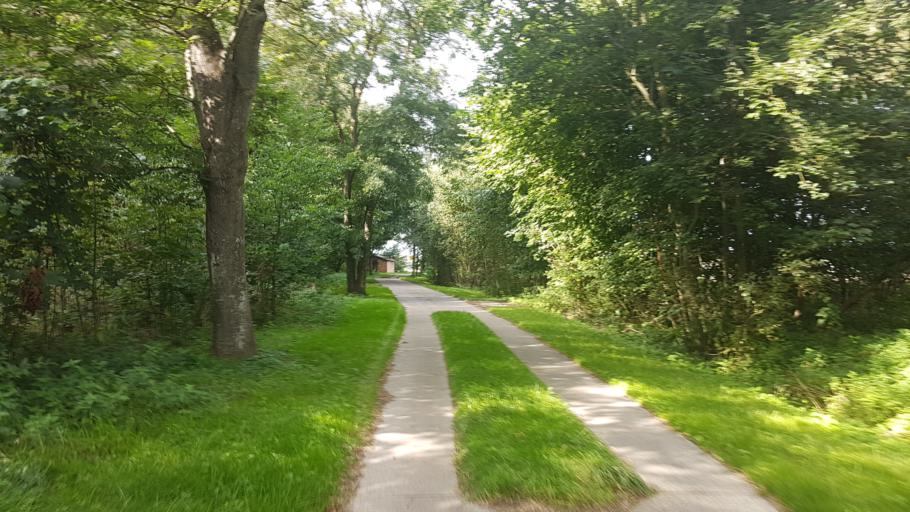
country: DE
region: Mecklenburg-Vorpommern
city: Gingst
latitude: 54.4420
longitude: 13.1852
